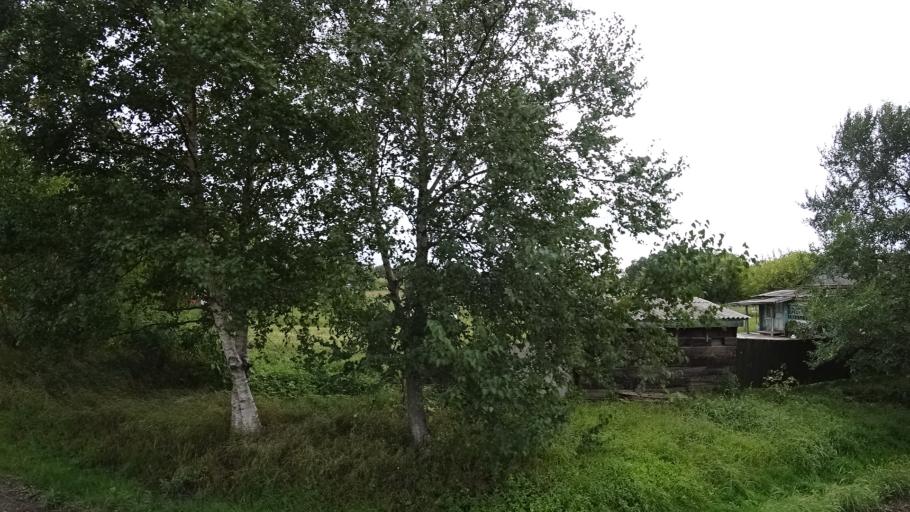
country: RU
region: Primorskiy
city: Chernigovka
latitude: 44.3331
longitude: 132.5678
